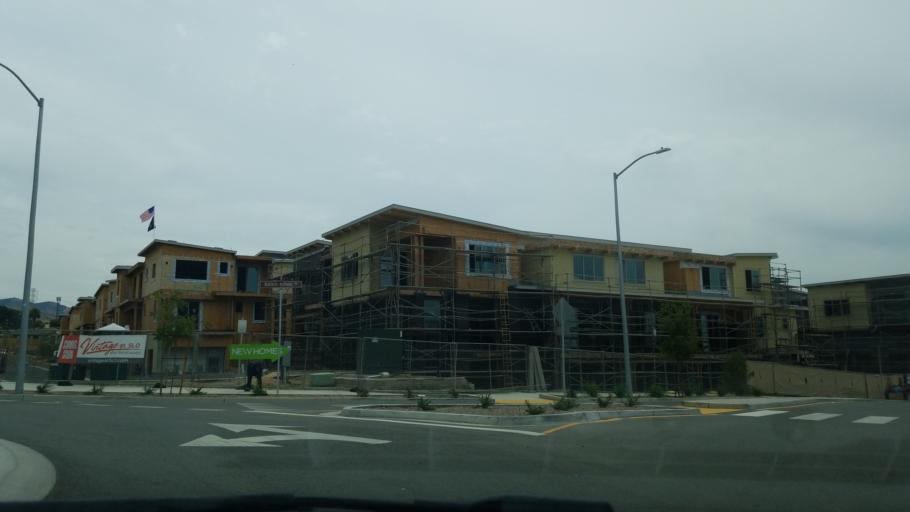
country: US
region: California
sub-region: San Luis Obispo County
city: San Luis Obispo
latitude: 35.2612
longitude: -120.6398
